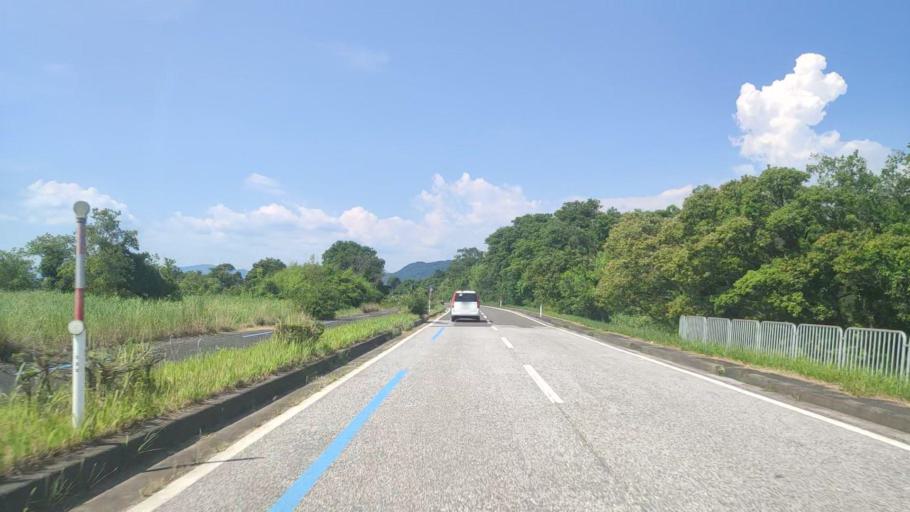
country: JP
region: Shiga Prefecture
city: Nagahama
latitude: 35.4286
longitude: 136.1968
